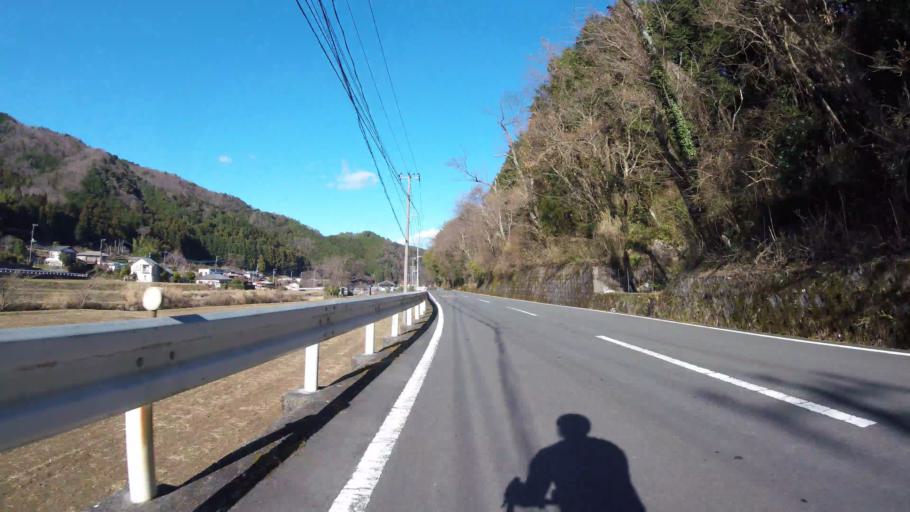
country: JP
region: Shizuoka
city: Ito
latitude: 34.9273
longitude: 138.9905
